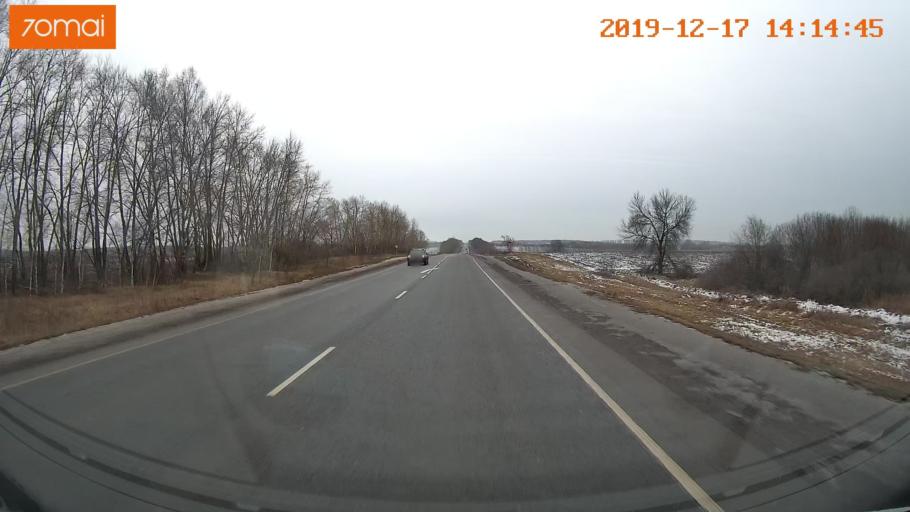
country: RU
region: Rjazan
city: Bagramovo
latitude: 54.5010
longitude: 39.4828
